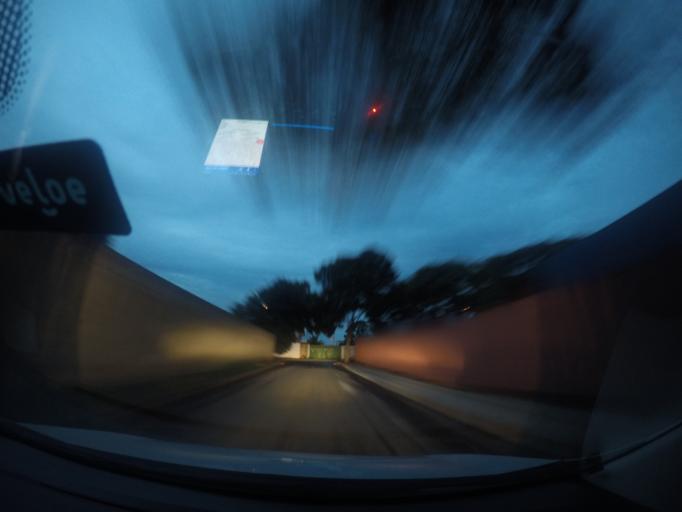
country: BR
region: Goias
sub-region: Goiania
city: Goiania
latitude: -16.6433
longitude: -49.2400
